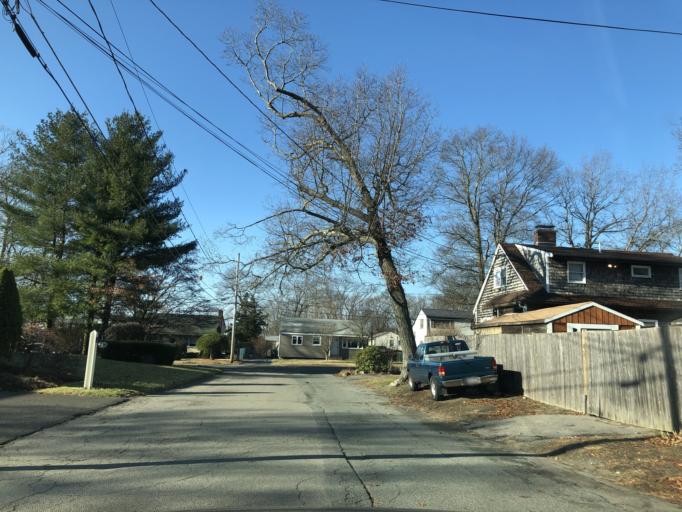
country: US
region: Massachusetts
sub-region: Plymouth County
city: Brockton
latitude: 42.1006
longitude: -71.0046
